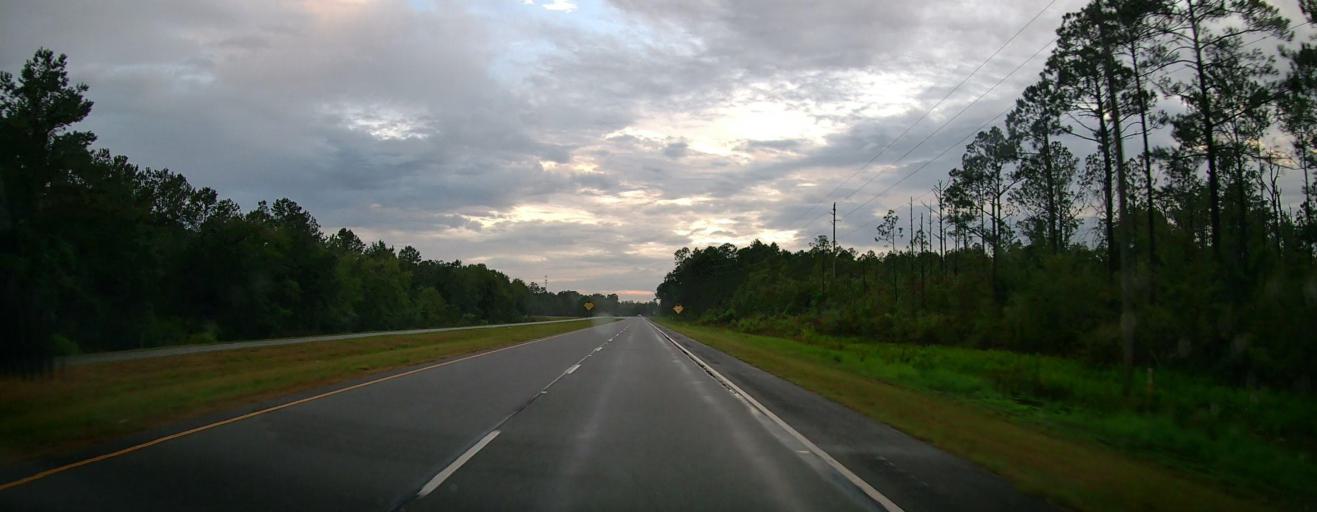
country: US
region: Georgia
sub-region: Lanier County
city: Lakeland
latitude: 30.9447
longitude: -82.9853
